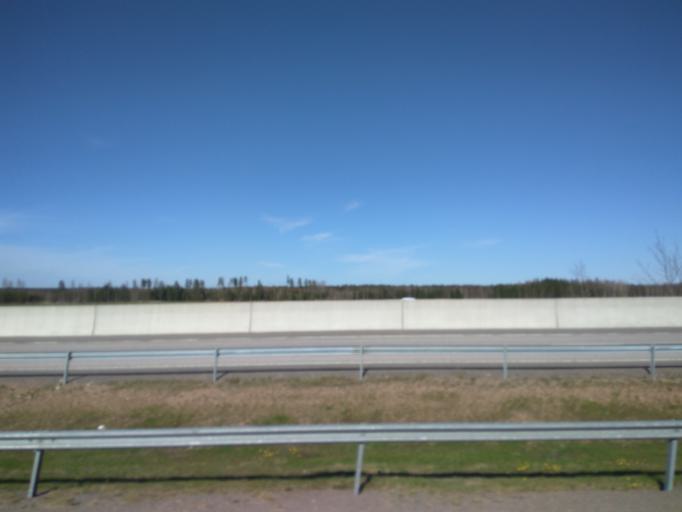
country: FI
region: Uusimaa
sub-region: Loviisa
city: Perna
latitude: 60.4707
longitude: 26.1246
